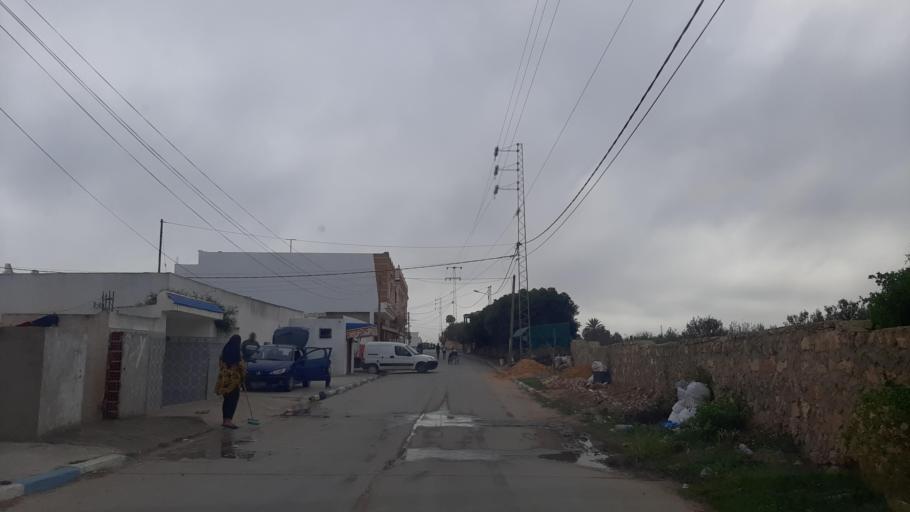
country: TN
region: Nabul
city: Menzel Heurr
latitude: 36.6812
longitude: 10.9260
